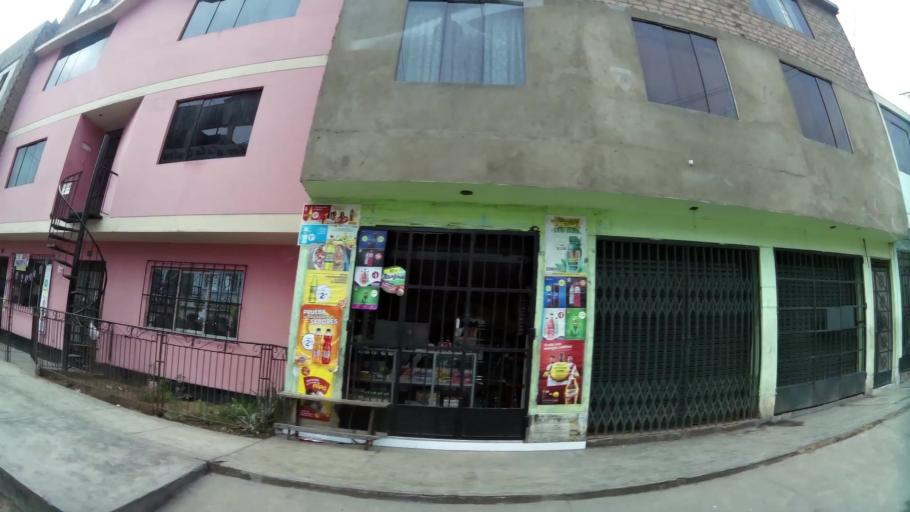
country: PE
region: Lima
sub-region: Lima
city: Independencia
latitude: -11.9774
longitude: -76.9963
